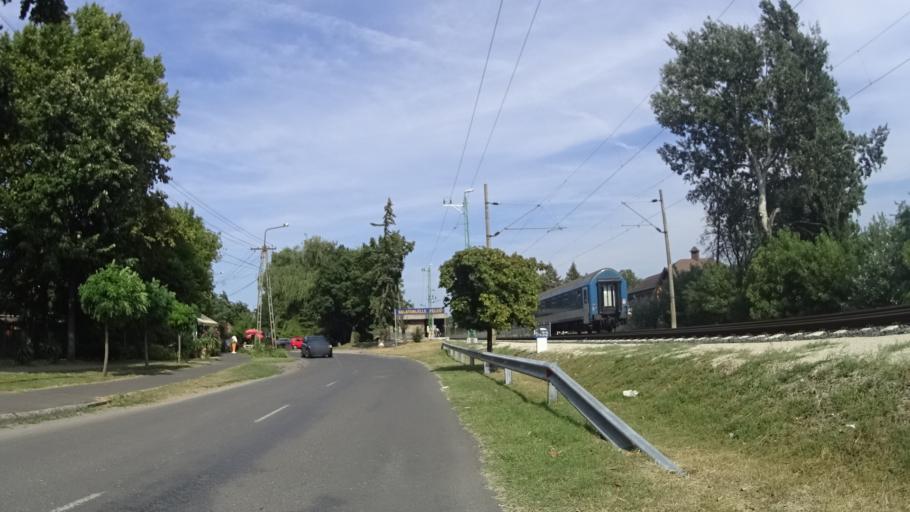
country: HU
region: Somogy
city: Balatonlelle
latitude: 46.7944
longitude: 17.7185
